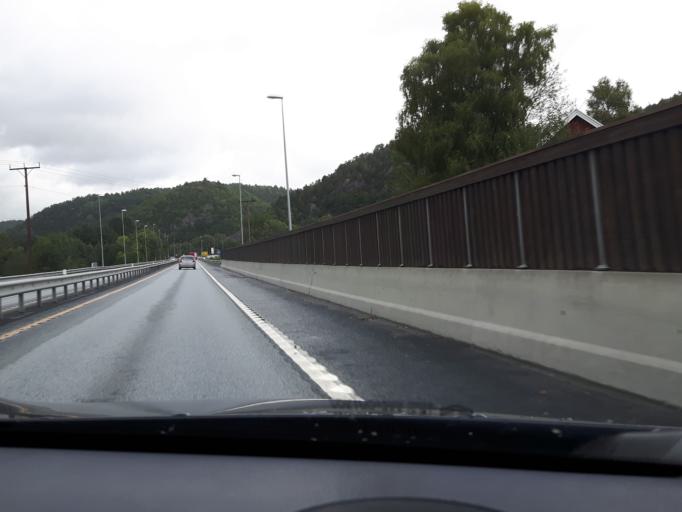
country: NO
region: Vest-Agder
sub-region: Songdalen
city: Nodeland
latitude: 58.1309
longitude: 7.8553
